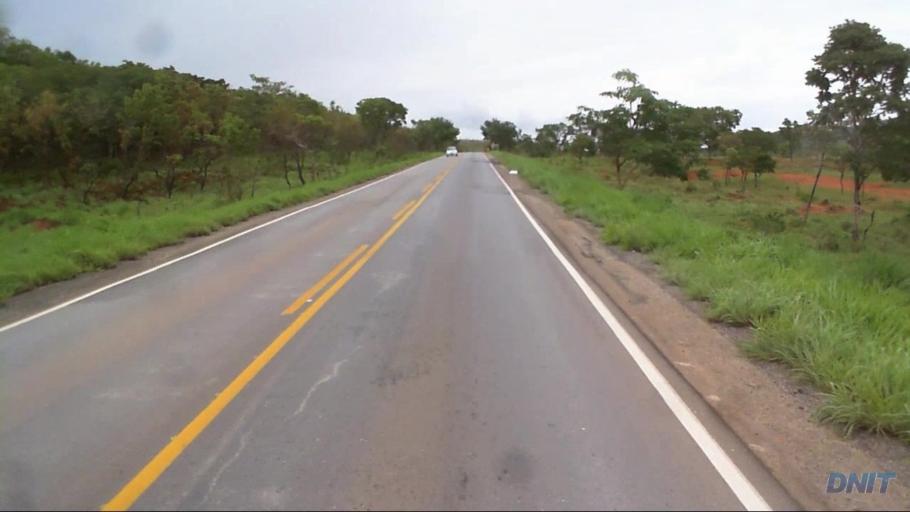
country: BR
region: Goias
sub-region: Padre Bernardo
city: Padre Bernardo
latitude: -15.4540
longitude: -48.2121
